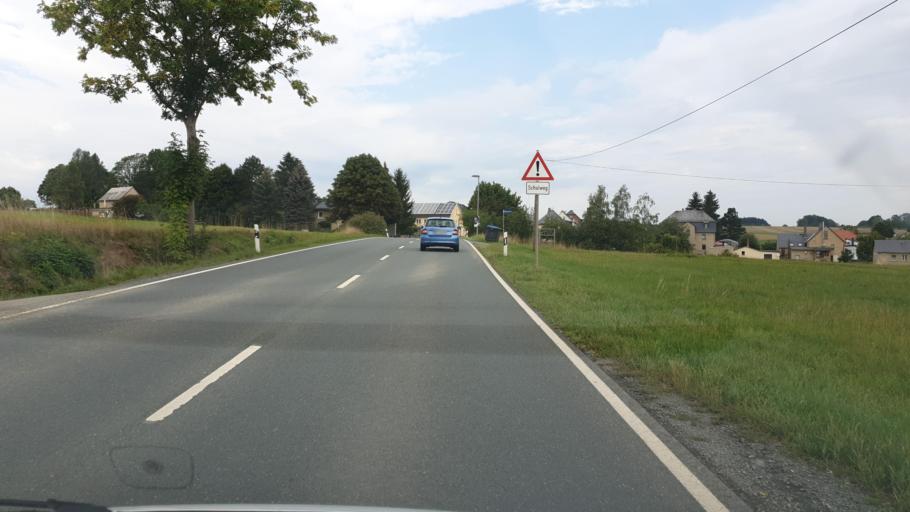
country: DE
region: Saxony
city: Lengenfeld
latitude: 50.5863
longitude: 12.3469
